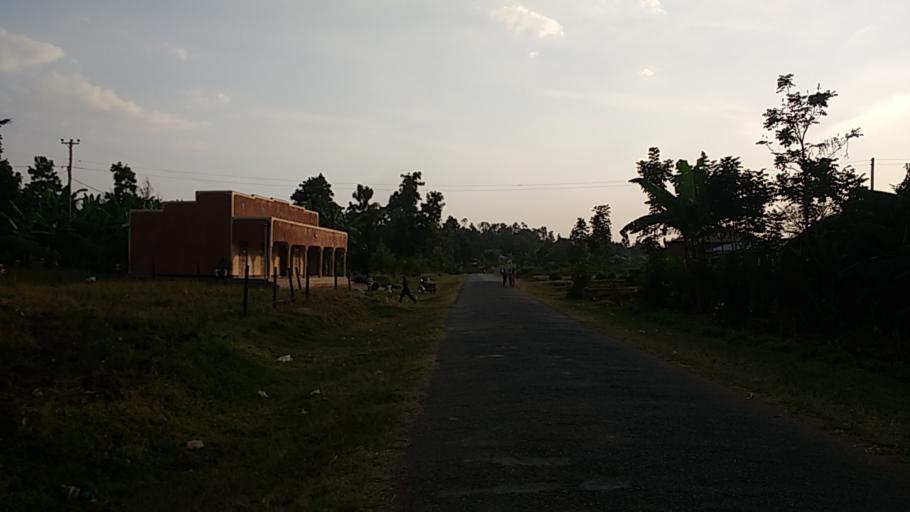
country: UG
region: Eastern Region
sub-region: Mbale District
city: Mbale
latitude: 1.0749
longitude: 34.2070
